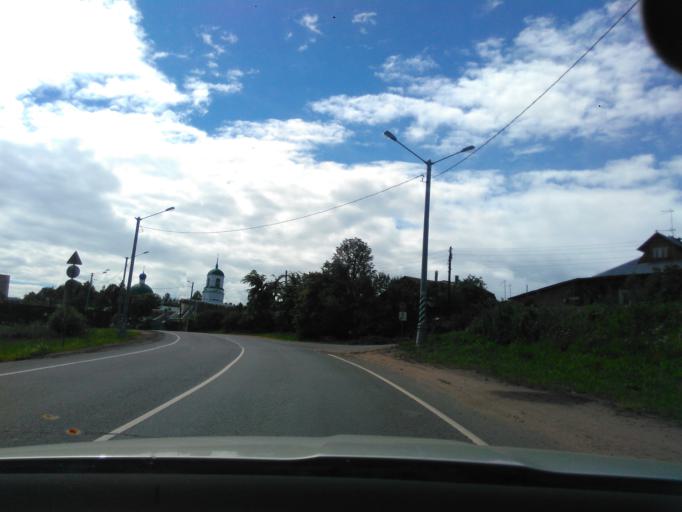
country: RU
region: Moskovskaya
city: Shevlyakovo
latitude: 56.4043
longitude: 36.8678
